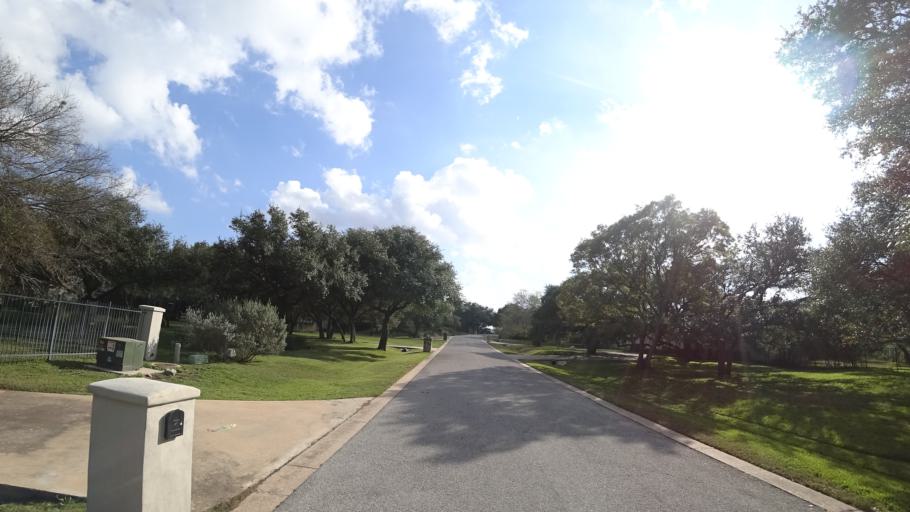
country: US
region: Texas
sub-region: Travis County
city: Barton Creek
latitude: 30.2847
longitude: -97.8813
